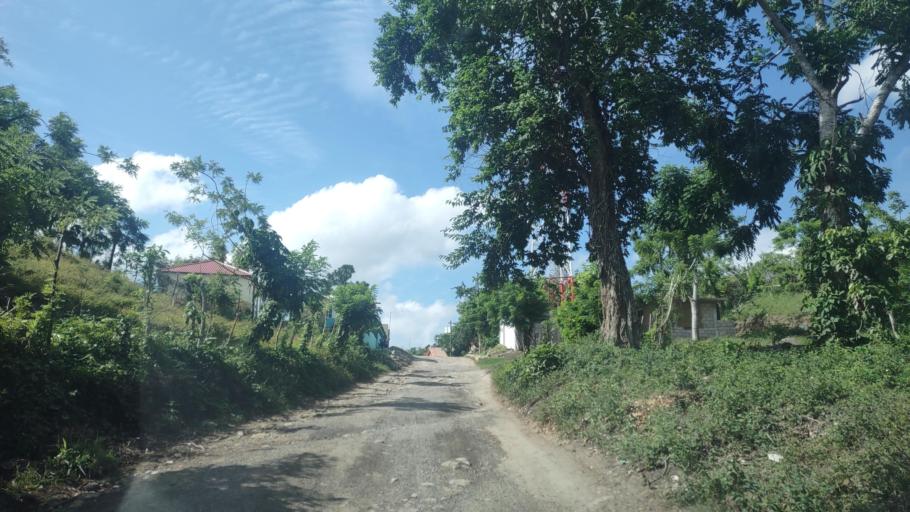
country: MM
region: Shan
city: Taunggyi
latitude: 20.5882
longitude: 97.3721
